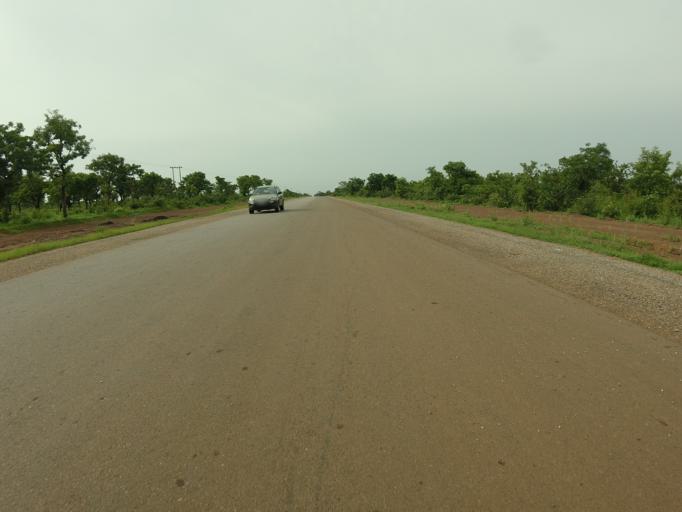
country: GH
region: Northern
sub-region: Yendi
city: Yendi
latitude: 9.6476
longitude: -0.0688
